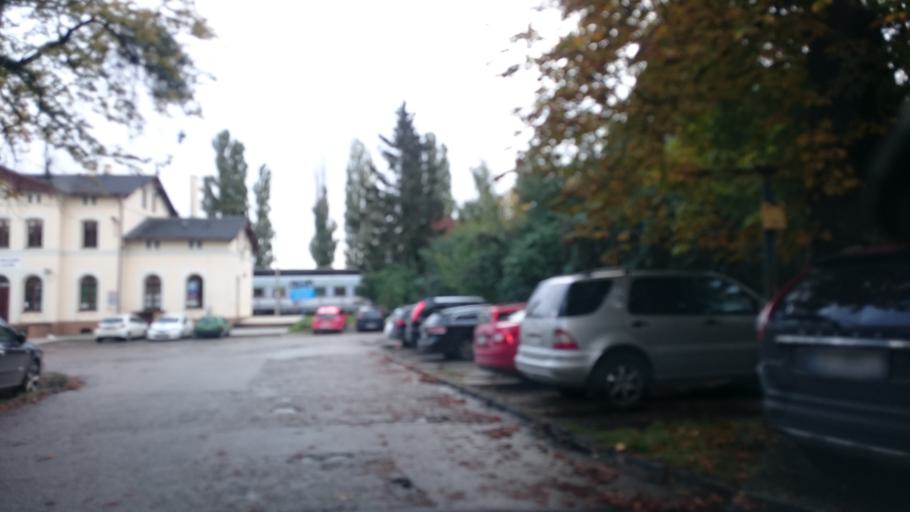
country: PL
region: Pomeranian Voivodeship
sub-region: Sopot
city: Sopot
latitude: 54.4097
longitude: 18.5707
